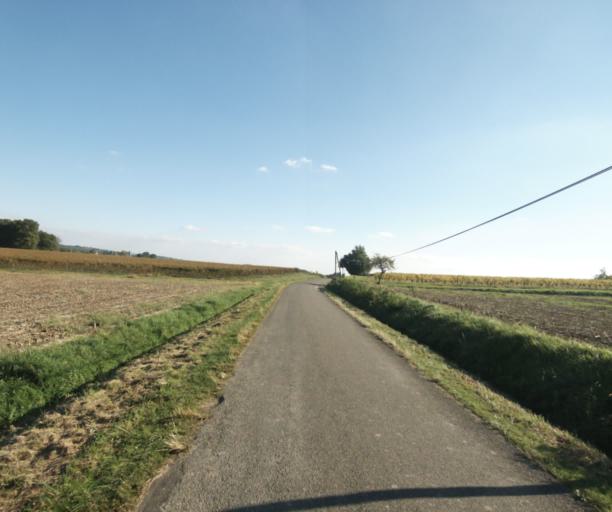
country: FR
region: Midi-Pyrenees
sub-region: Departement du Gers
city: Eauze
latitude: 43.8029
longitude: 0.1332
